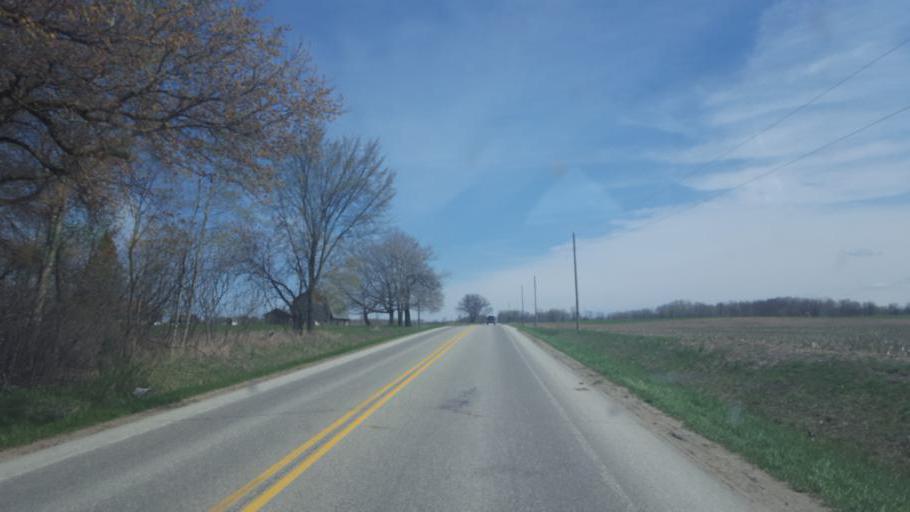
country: US
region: Michigan
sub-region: Midland County
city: Coleman
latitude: 43.8731
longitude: -84.6456
